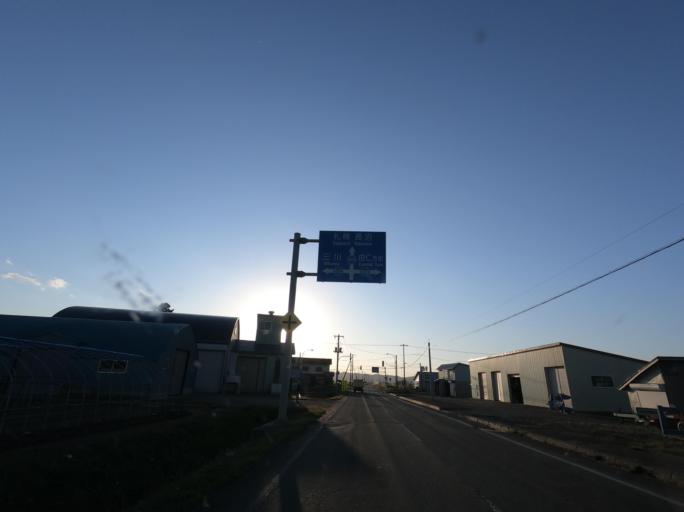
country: JP
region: Hokkaido
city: Iwamizawa
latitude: 42.9790
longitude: 141.8359
